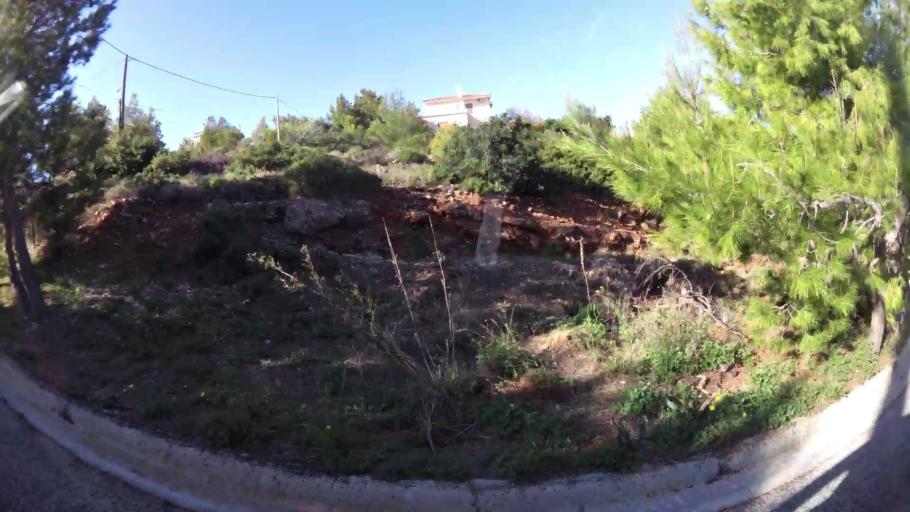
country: GR
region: Attica
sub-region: Nomarchia Anatolikis Attikis
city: Dhrafi
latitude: 38.0279
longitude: 23.9051
